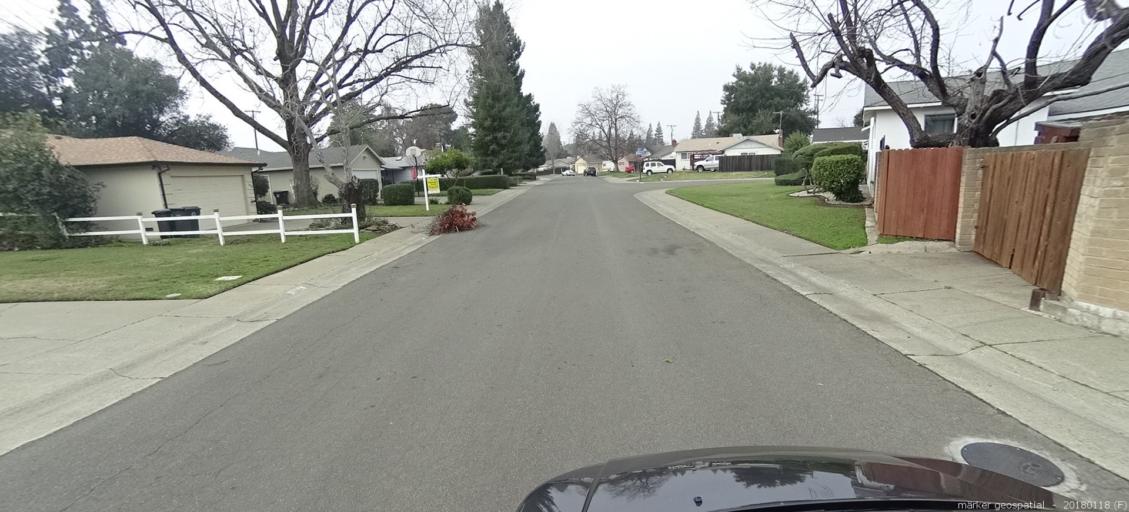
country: US
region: California
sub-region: Sacramento County
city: Rancho Cordova
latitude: 38.5951
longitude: -121.3066
